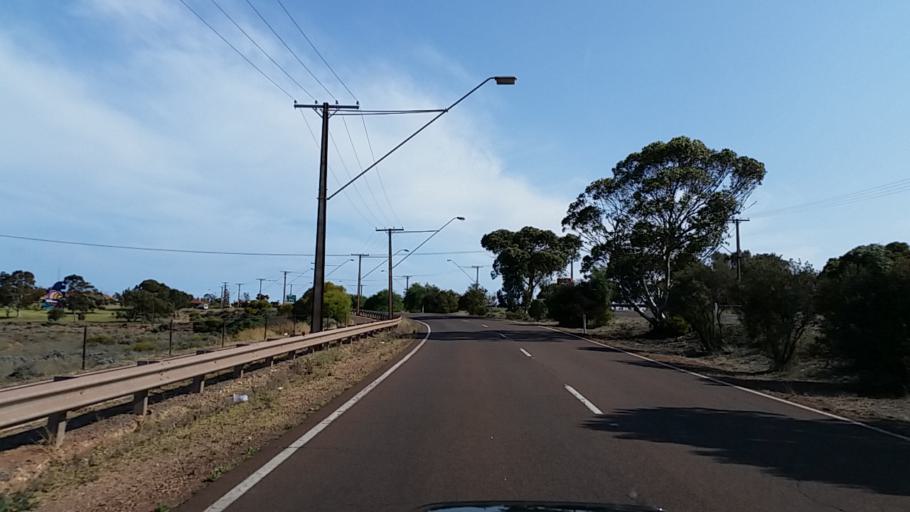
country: AU
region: South Australia
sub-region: Whyalla
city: Whyalla
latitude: -33.0227
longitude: 137.5731
